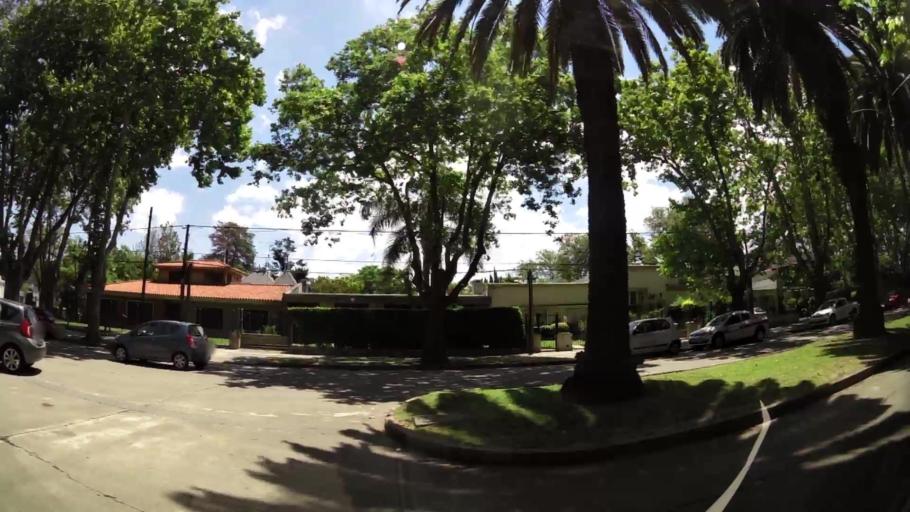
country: UY
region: Montevideo
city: Montevideo
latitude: -34.8660
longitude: -56.1983
